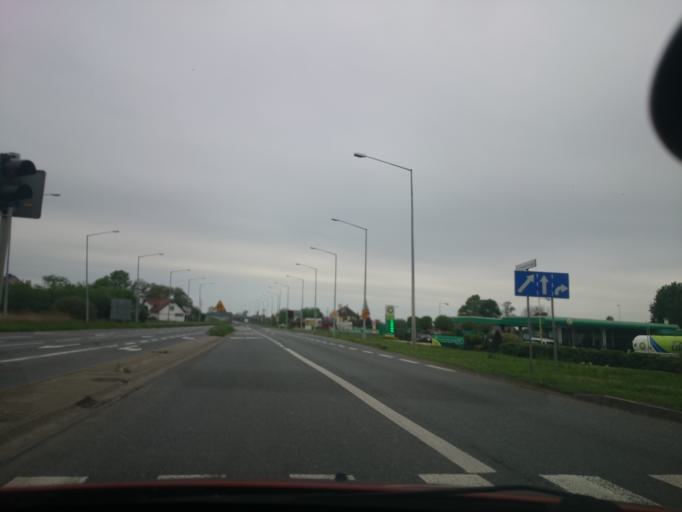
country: PL
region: Opole Voivodeship
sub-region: Powiat opolski
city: Opole
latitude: 50.7038
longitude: 17.9340
